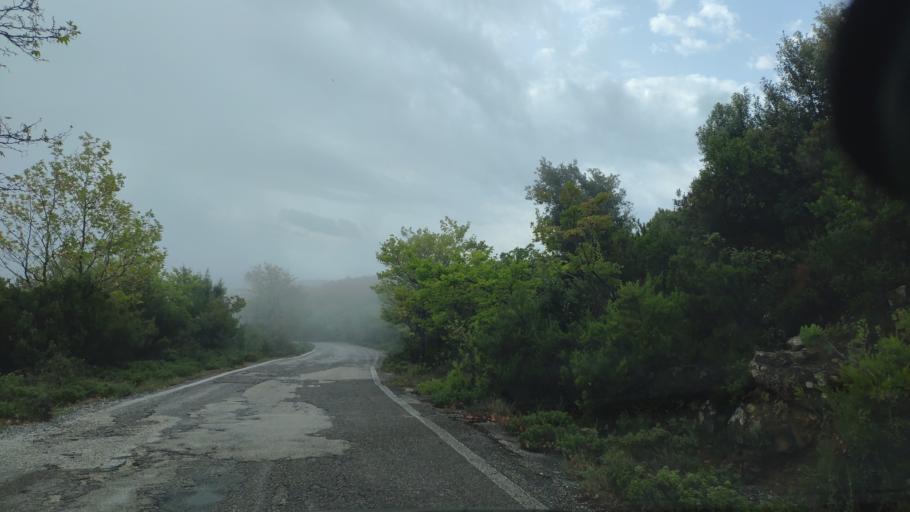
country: GR
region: West Greece
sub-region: Nomos Aitolias kai Akarnanias
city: Sardinia
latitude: 38.8486
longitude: 21.3158
